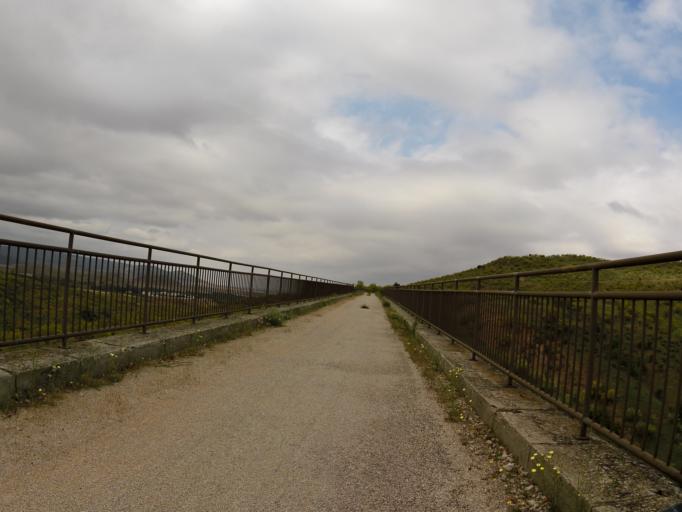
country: ES
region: Castille-La Mancha
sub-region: Provincia de Albacete
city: Alcaraz
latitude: 38.7013
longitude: -2.4937
